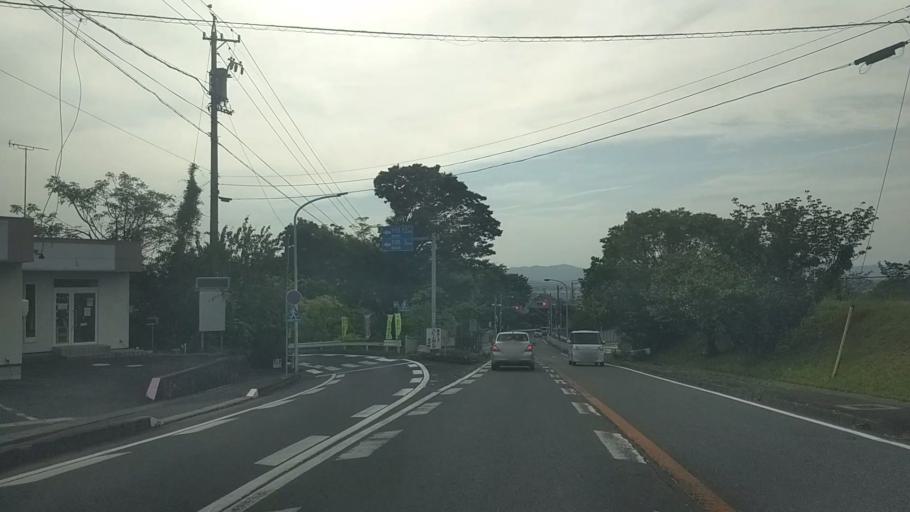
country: JP
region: Shizuoka
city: Kosai-shi
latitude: 34.7598
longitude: 137.6187
